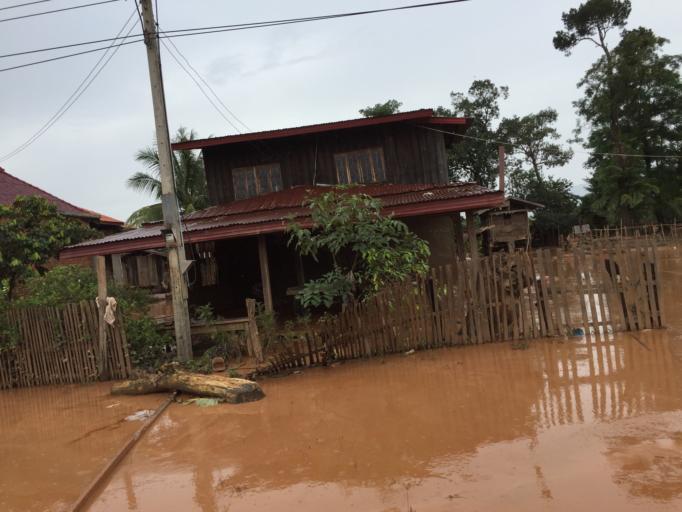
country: LA
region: Attapu
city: Attapu
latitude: 14.7016
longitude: 106.5296
